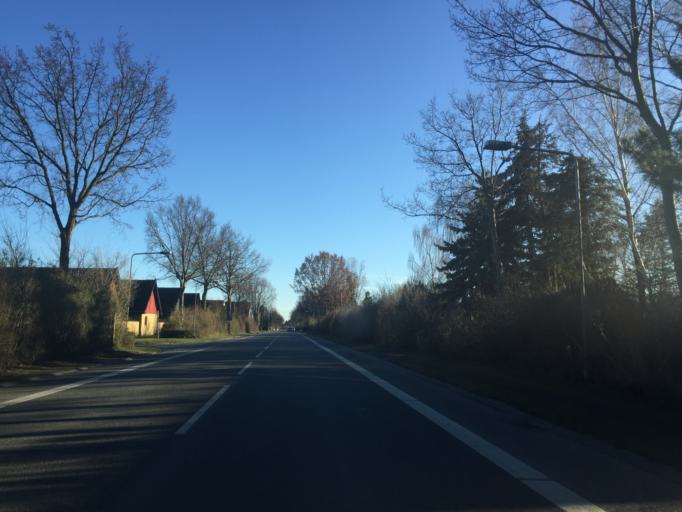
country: DK
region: Capital Region
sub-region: Dragor Kommune
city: Dragor
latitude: 55.5975
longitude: 12.6583
